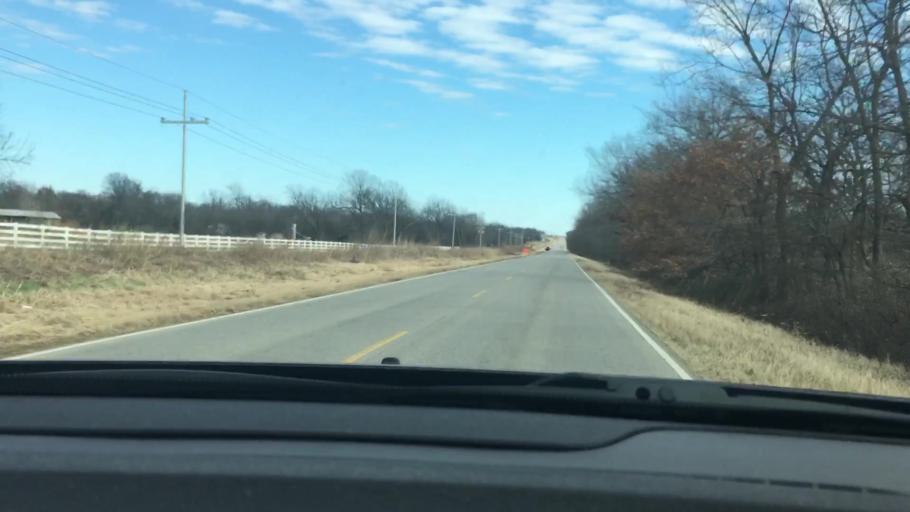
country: US
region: Oklahoma
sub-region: Garvin County
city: Stratford
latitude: 34.7967
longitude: -96.8739
